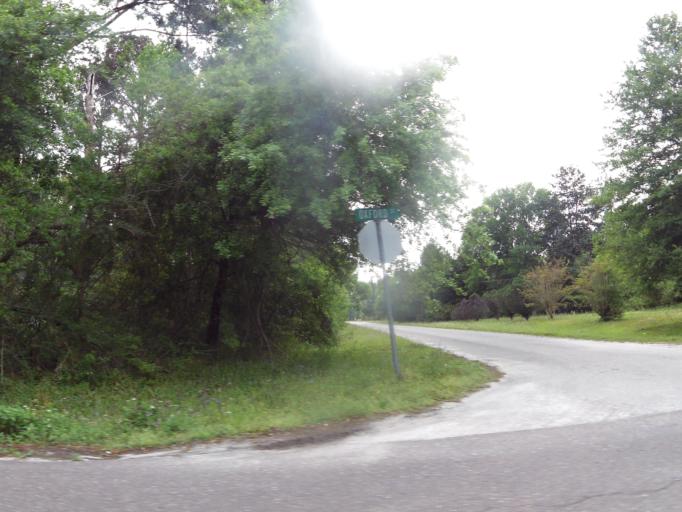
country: US
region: Florida
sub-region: Nassau County
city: Hilliard
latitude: 30.6942
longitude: -81.9248
